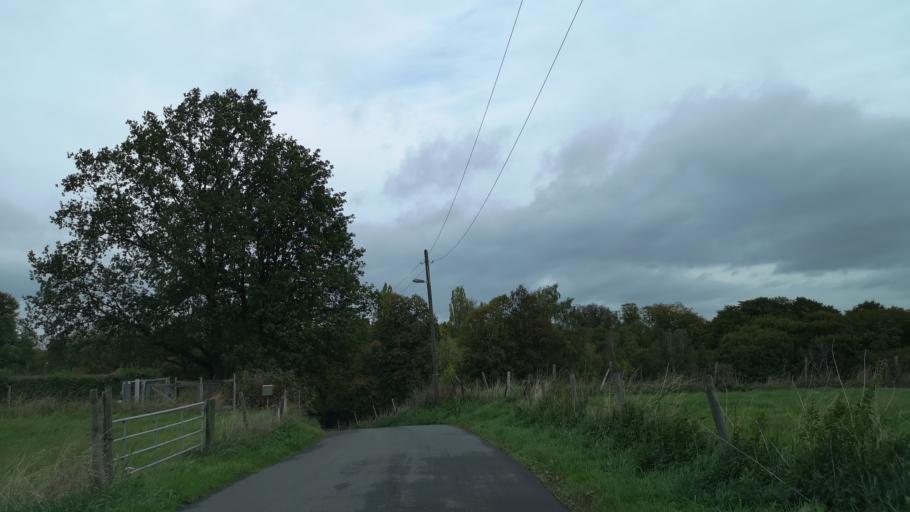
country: DE
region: North Rhine-Westphalia
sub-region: Regierungsbezirk Dusseldorf
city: Velbert
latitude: 51.3761
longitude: 7.0840
